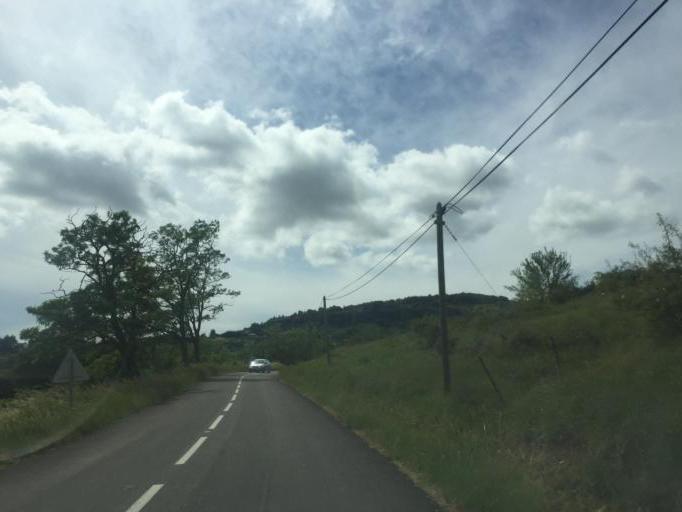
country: FR
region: Rhone-Alpes
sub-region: Departement de l'Ardeche
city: Villeneuve-de-Berg
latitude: 44.6023
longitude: 4.5374
